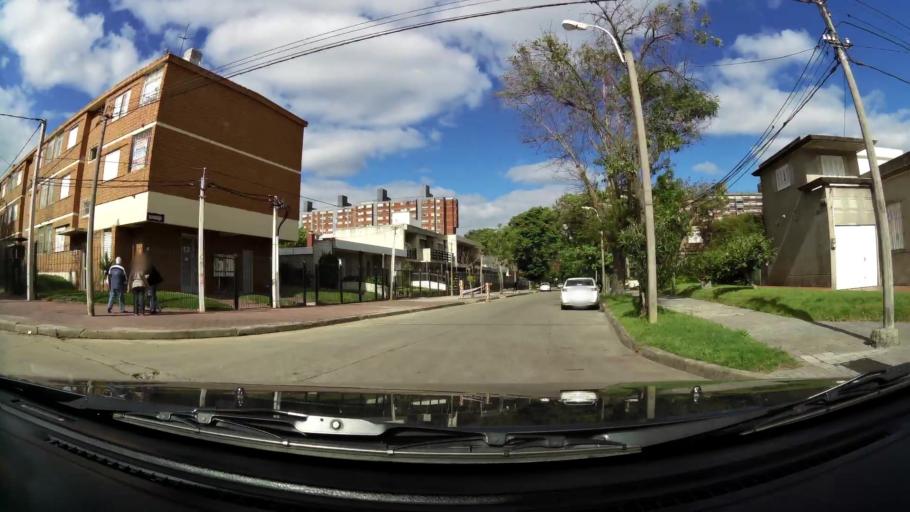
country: UY
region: Montevideo
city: Montevideo
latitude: -34.8790
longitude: -56.1639
